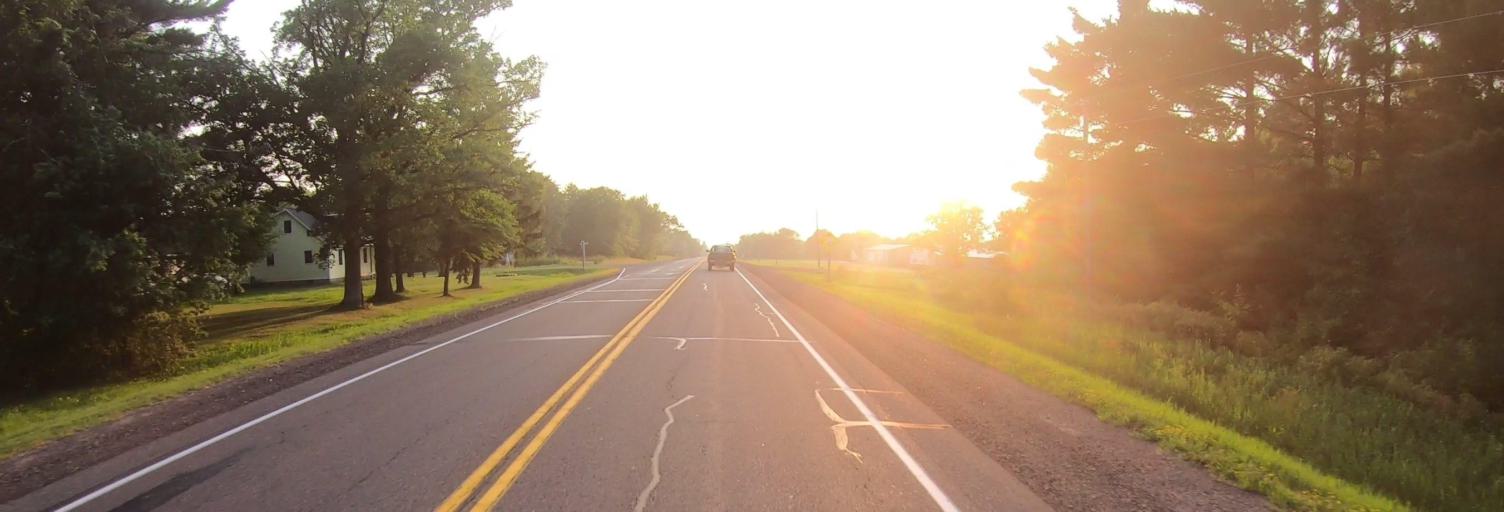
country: US
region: Wisconsin
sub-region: Polk County
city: Frederic
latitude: 45.7719
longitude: -92.5129
